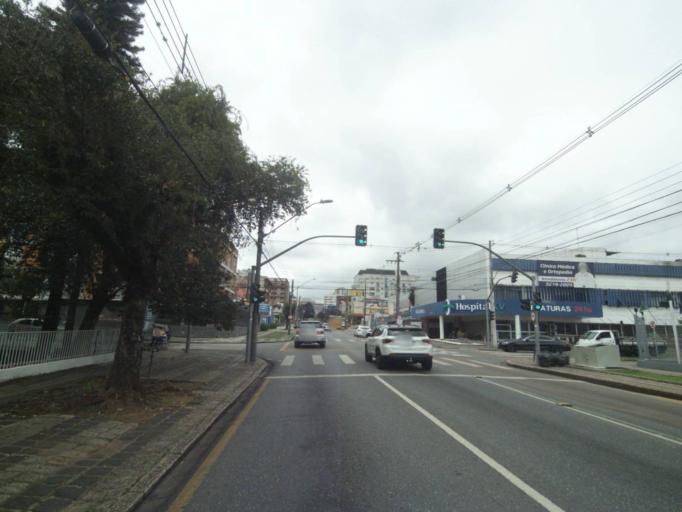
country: BR
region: Parana
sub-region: Curitiba
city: Curitiba
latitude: -25.4269
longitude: -49.2523
